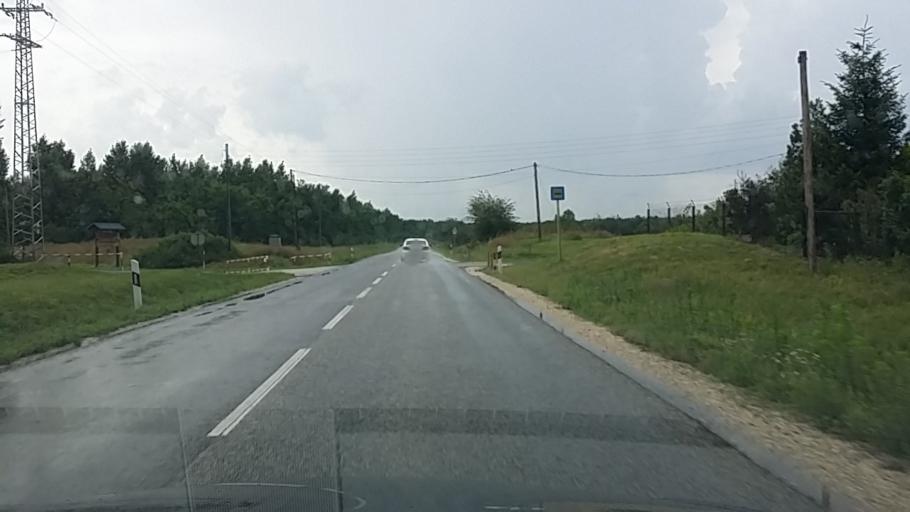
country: HU
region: Pest
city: Inarcs
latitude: 47.3278
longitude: 19.3049
